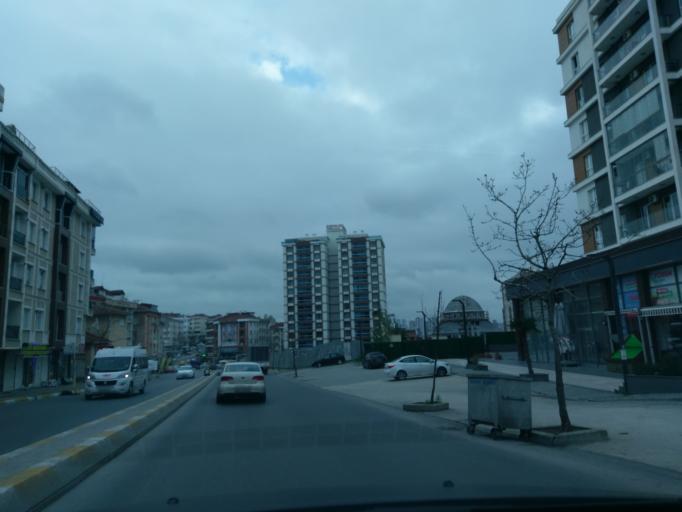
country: TR
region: Istanbul
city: Esenyurt
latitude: 41.0112
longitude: 28.6681
